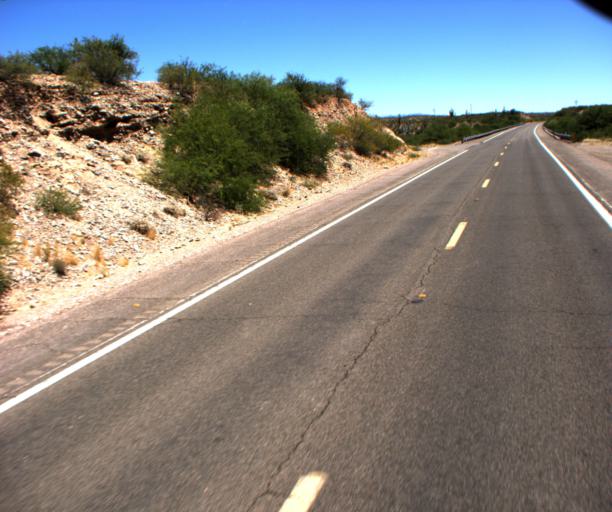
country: US
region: Arizona
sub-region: Pinal County
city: Mammoth
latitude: 32.8169
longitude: -110.6904
